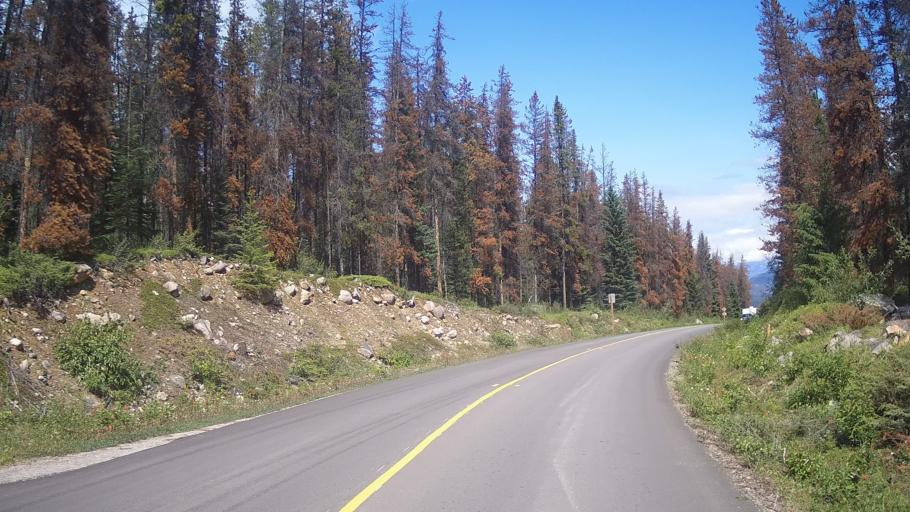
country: CA
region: Alberta
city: Jasper Park Lodge
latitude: 52.7749
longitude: -118.0327
